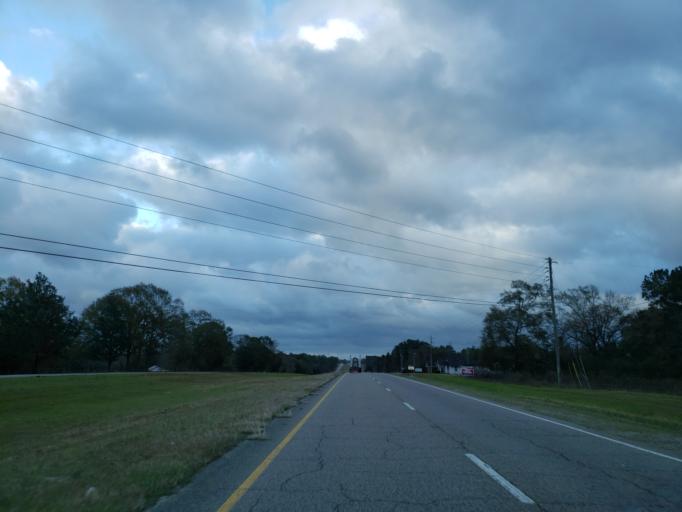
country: US
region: Mississippi
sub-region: George County
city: Lucedale
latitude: 30.9204
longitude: -88.5041
